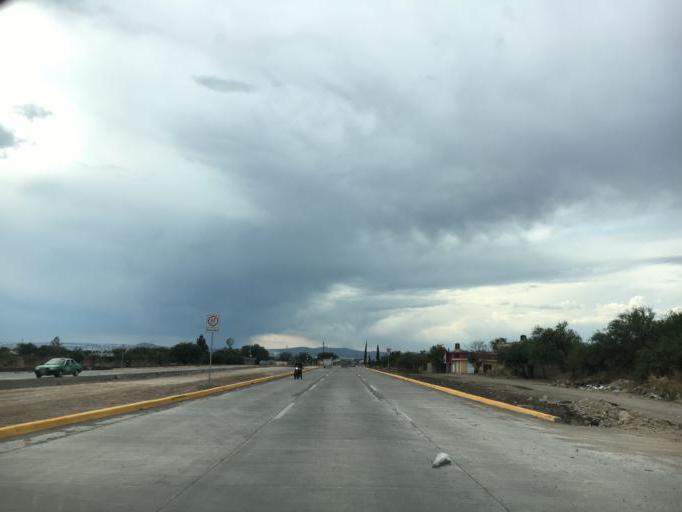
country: MX
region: Guanajuato
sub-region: Leon
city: Fraccionamiento Paraiso Real
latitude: 21.1078
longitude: -101.5819
